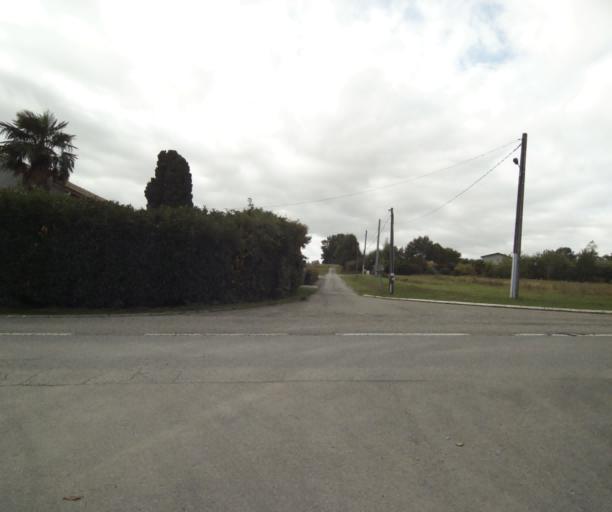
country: FR
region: Midi-Pyrenees
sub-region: Departement du Tarn-et-Garonne
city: Beaumont-de-Lomagne
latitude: 43.8624
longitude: 1.1010
